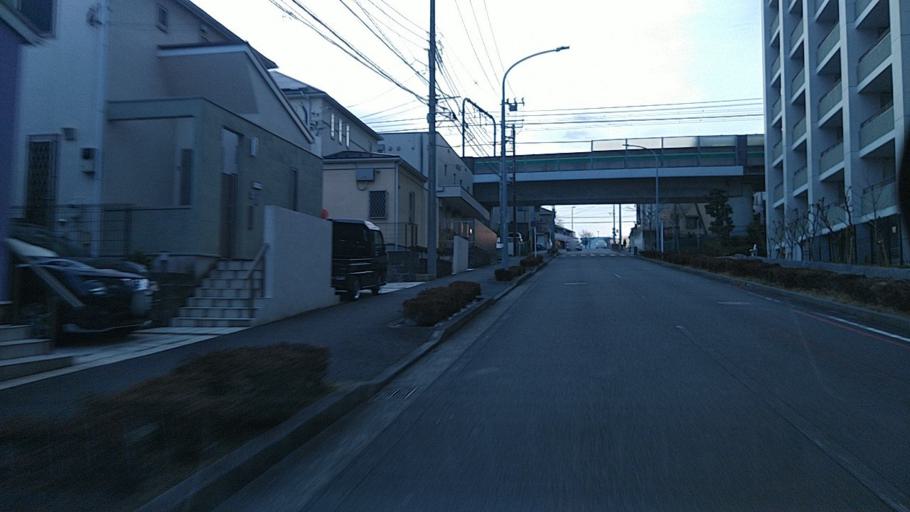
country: JP
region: Kanagawa
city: Fujisawa
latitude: 35.4120
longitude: 139.4877
